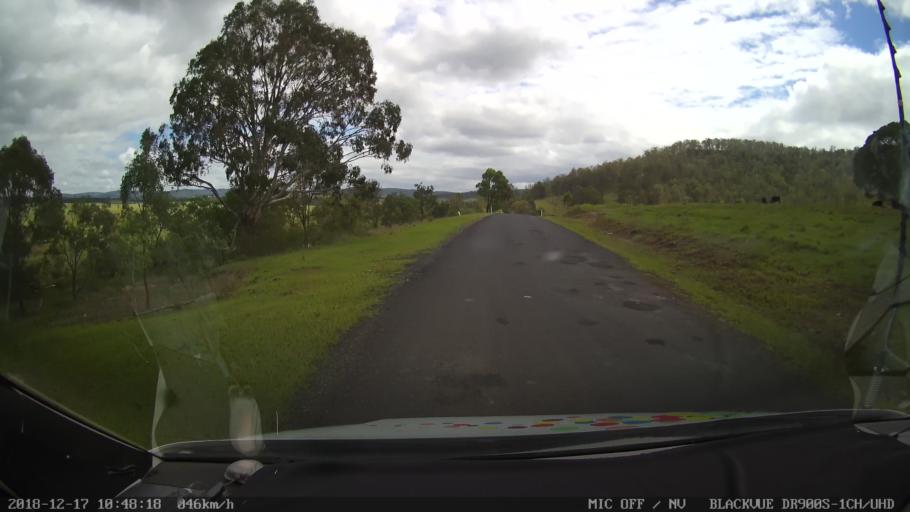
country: AU
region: New South Wales
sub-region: Clarence Valley
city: Gordon
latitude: -28.8741
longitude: 152.5707
